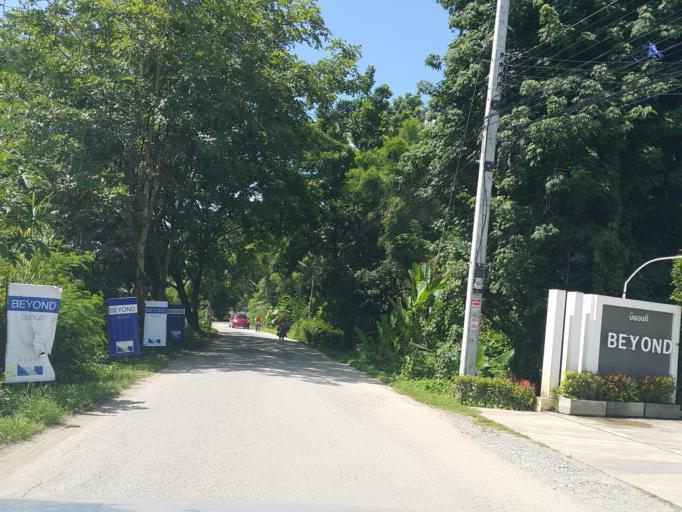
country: TH
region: Chiang Mai
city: San Kamphaeng
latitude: 18.7253
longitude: 99.0988
